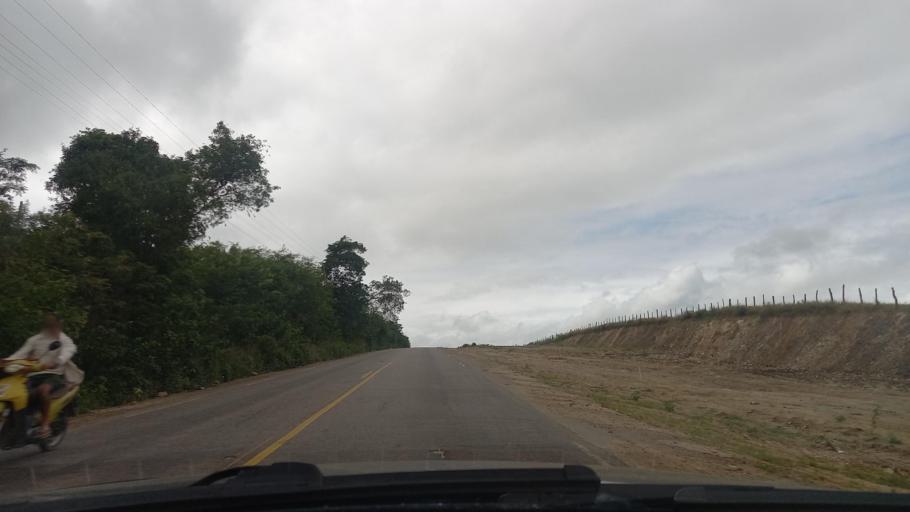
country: BR
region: Alagoas
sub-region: Batalha
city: Batalha
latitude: -9.6440
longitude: -37.1911
